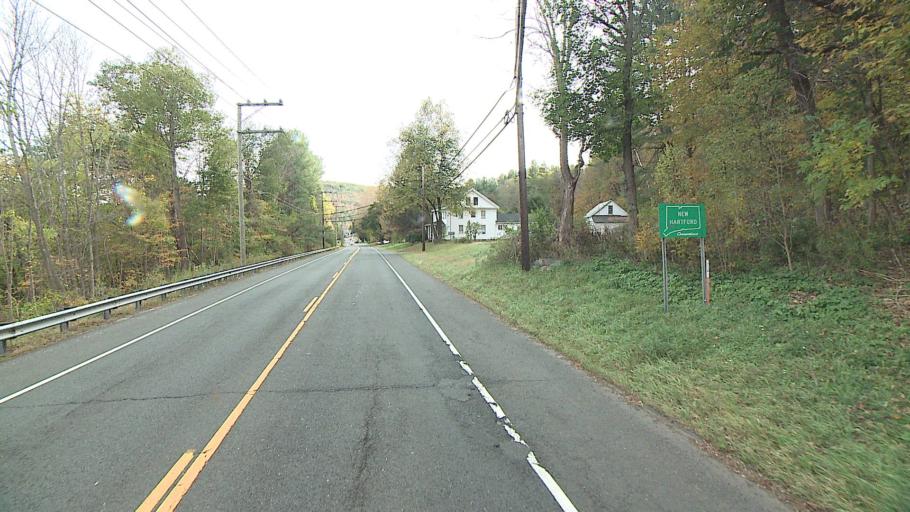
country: US
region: Connecticut
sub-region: Litchfield County
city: New Hartford Center
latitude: 41.8849
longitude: -72.9831
